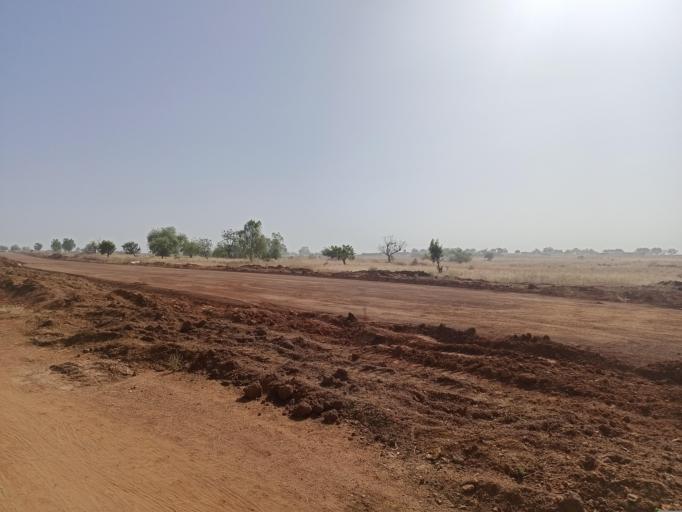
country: BF
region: Centre-Est
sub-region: Province du Boulgou
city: Tenkodogo
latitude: 11.5326
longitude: -0.4841
